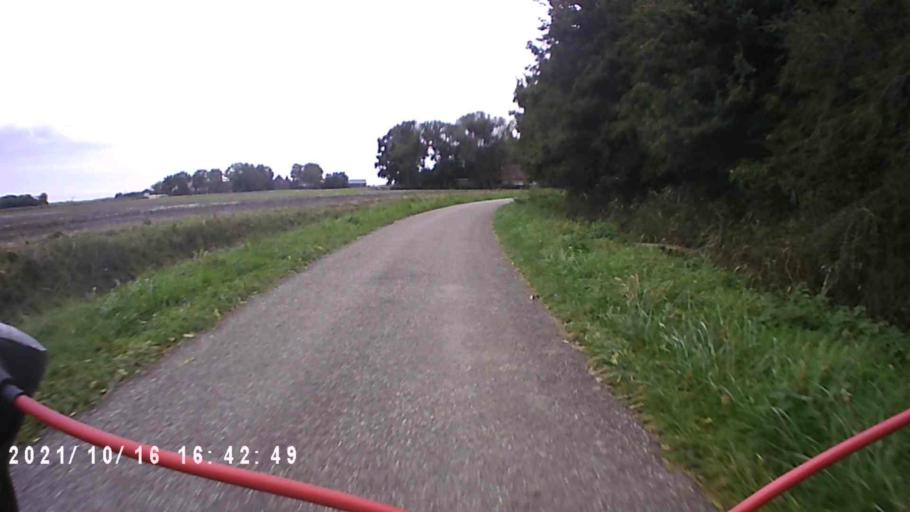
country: NL
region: Friesland
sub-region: Gemeente Dongeradeel
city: Anjum
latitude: 53.3727
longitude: 6.1437
